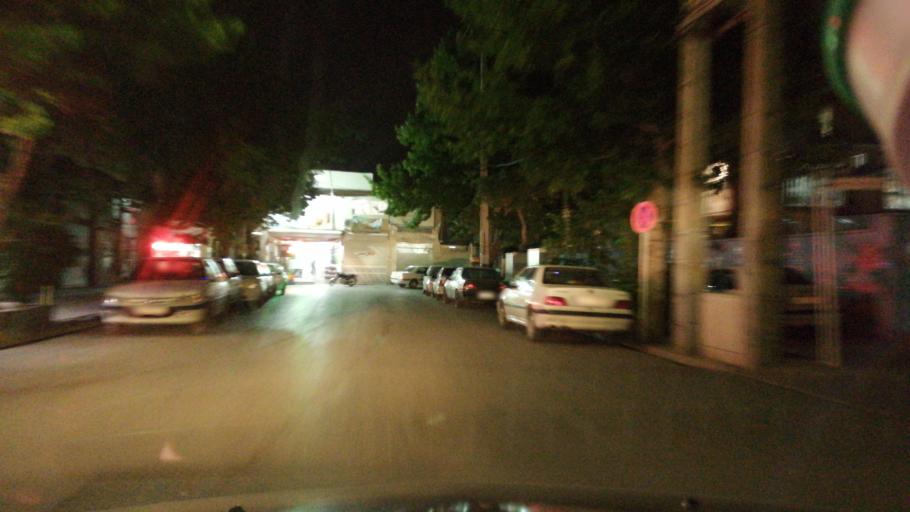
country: IR
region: Razavi Khorasan
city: Mashhad
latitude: 36.3072
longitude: 59.6046
